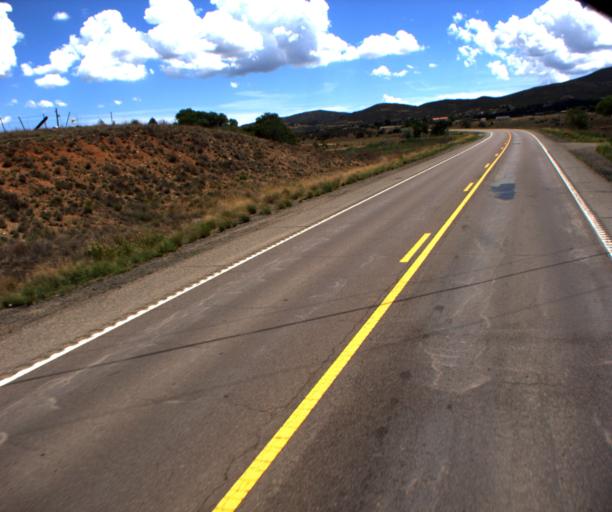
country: US
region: Arizona
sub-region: Yavapai County
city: Dewey-Humboldt
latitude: 34.5294
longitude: -112.2295
